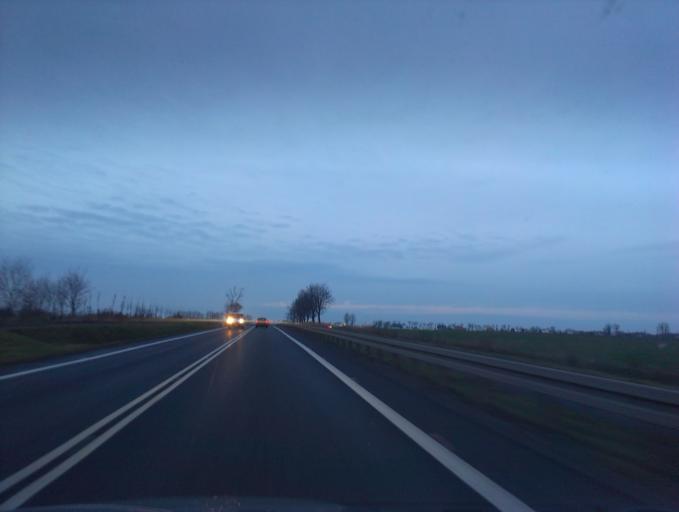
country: PL
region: Greater Poland Voivodeship
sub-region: Powiat poznanski
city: Zlotniki
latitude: 52.5711
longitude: 16.8328
